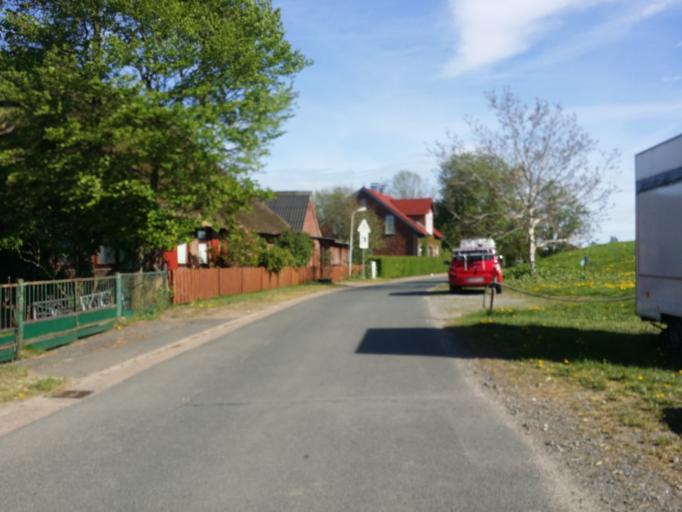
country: DE
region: Lower Saxony
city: Lemwerder
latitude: 53.1364
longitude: 8.6382
